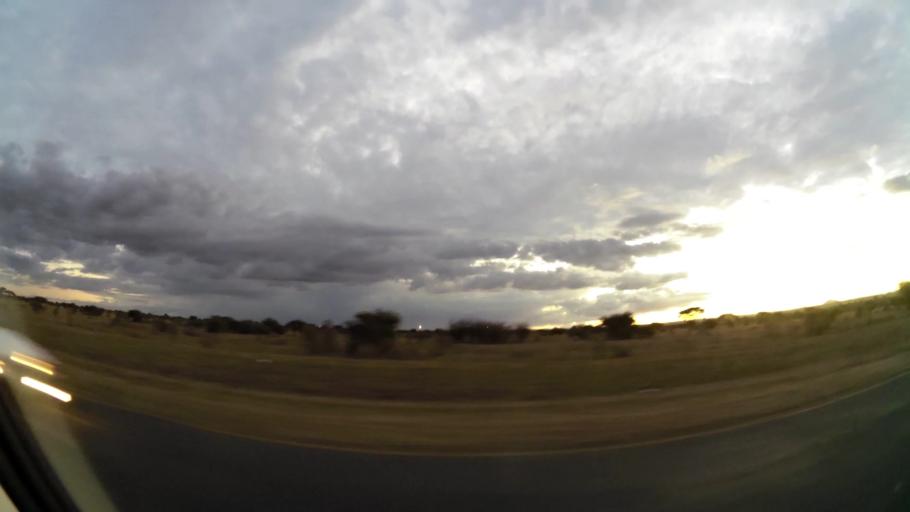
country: ZA
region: Limpopo
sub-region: Capricorn District Municipality
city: Polokwane
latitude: -23.8316
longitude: 29.4263
